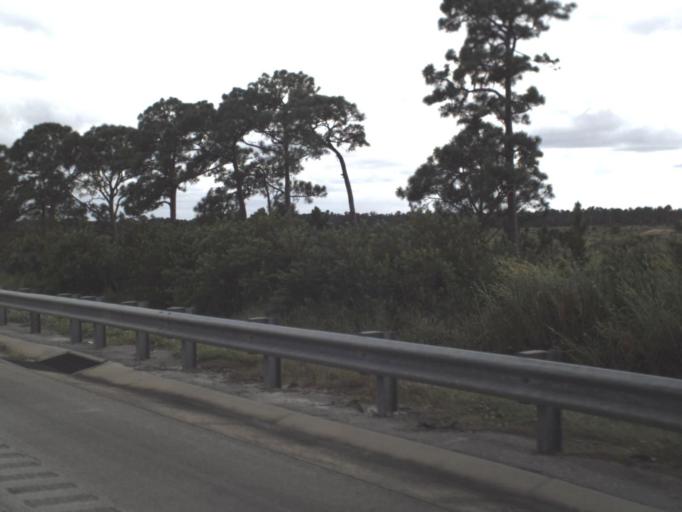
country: US
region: Florida
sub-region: Palm Beach County
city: Limestone Creek
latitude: 26.9794
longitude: -80.1839
